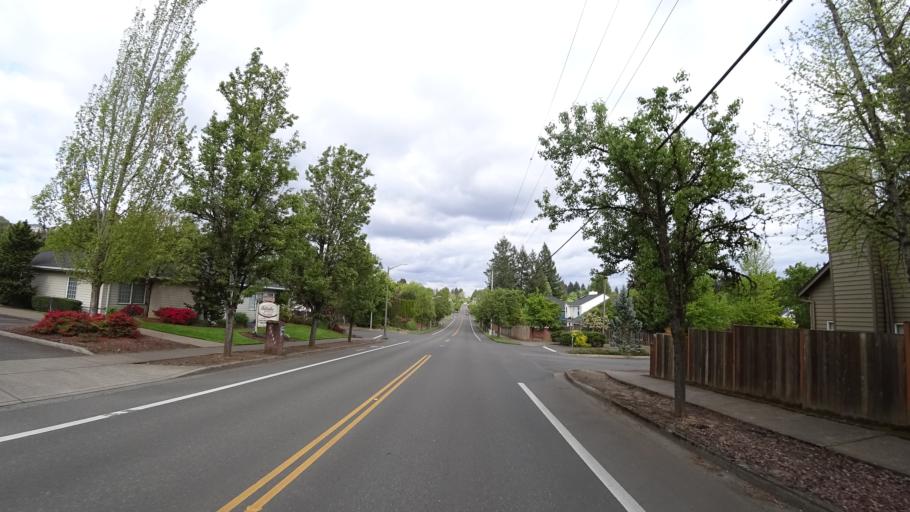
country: US
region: Oregon
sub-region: Washington County
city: Beaverton
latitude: 45.4530
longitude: -122.8327
